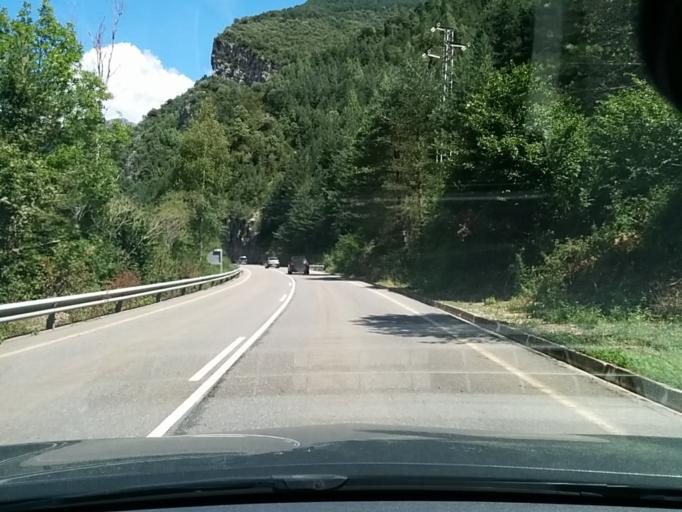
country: ES
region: Aragon
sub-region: Provincia de Huesca
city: Bielsa
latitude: 42.5996
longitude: 0.2396
